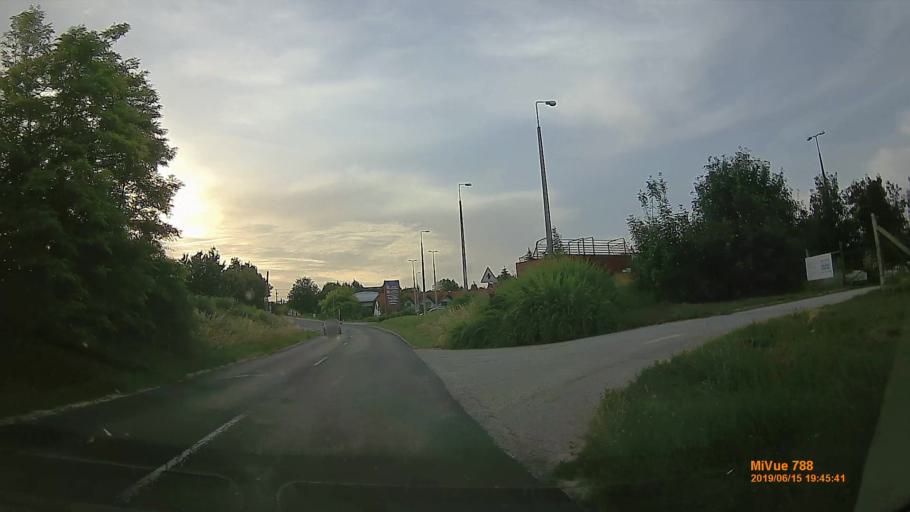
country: HU
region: Veszprem
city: Szentkiralyszabadja
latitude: 47.0114
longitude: 17.9621
